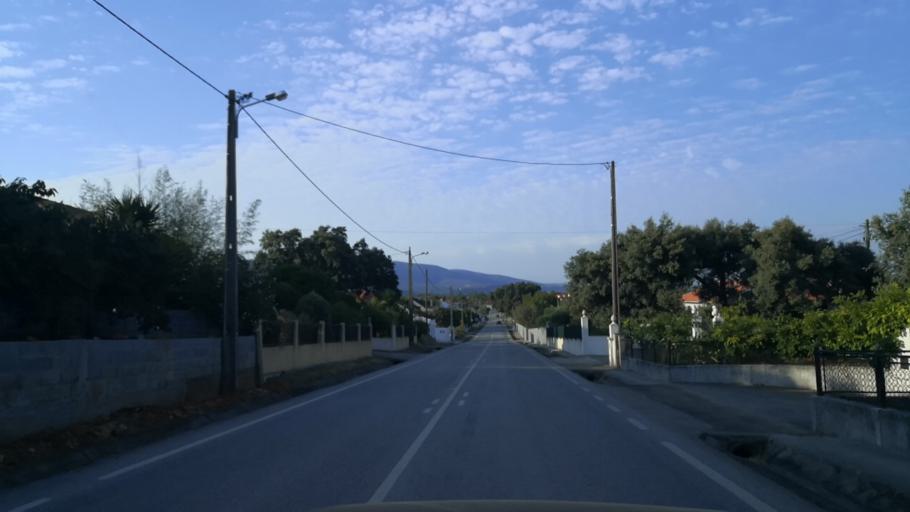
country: PT
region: Santarem
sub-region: Alcanena
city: Alcanena
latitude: 39.4468
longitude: -8.6232
